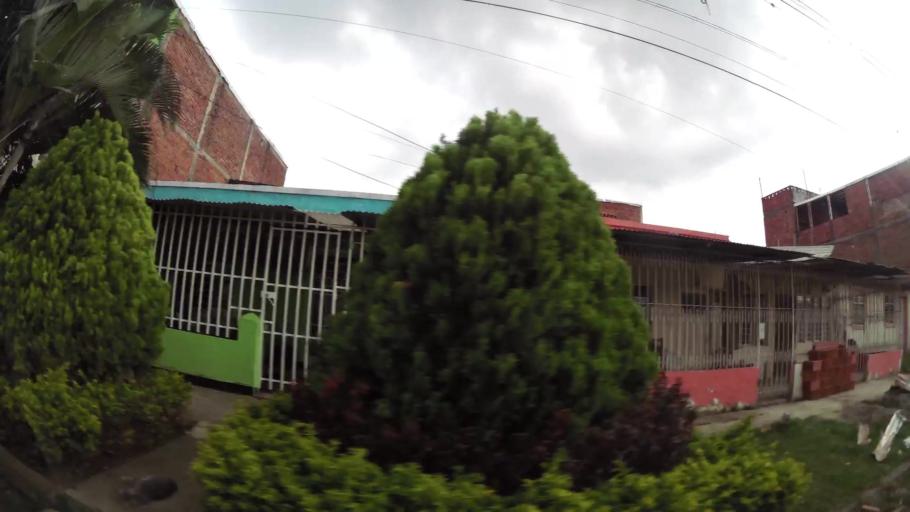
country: CO
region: Valle del Cauca
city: Cali
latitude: 3.4610
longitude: -76.4900
